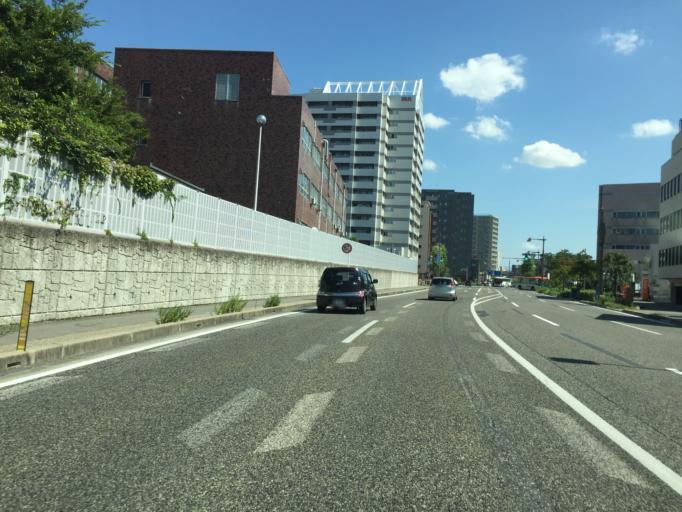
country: JP
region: Niigata
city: Niigata-shi
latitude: 37.9174
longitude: 139.0352
